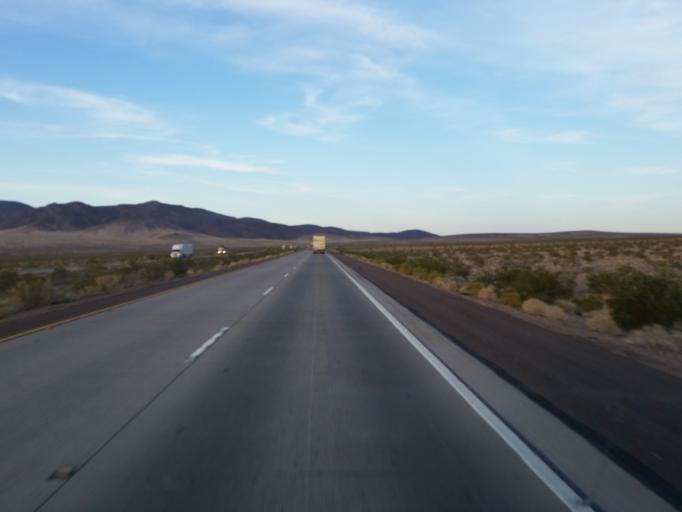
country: US
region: California
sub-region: San Bernardino County
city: Twentynine Palms
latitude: 34.7267
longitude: -116.1209
